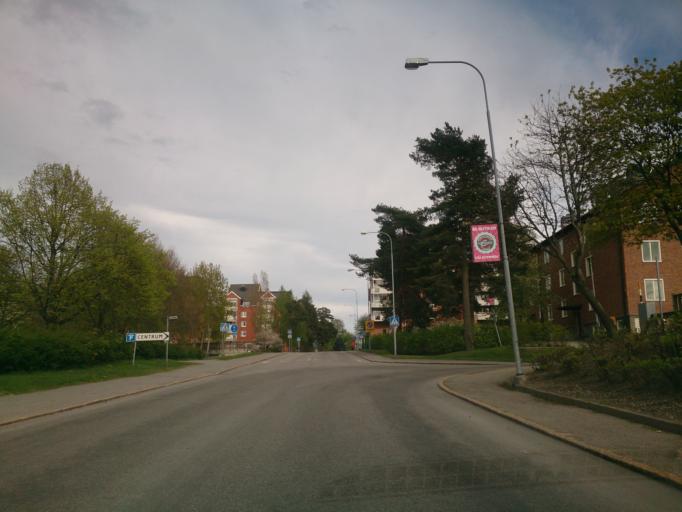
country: SE
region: Stockholm
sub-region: Haninge Kommun
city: Handen
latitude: 59.1723
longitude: 18.1403
